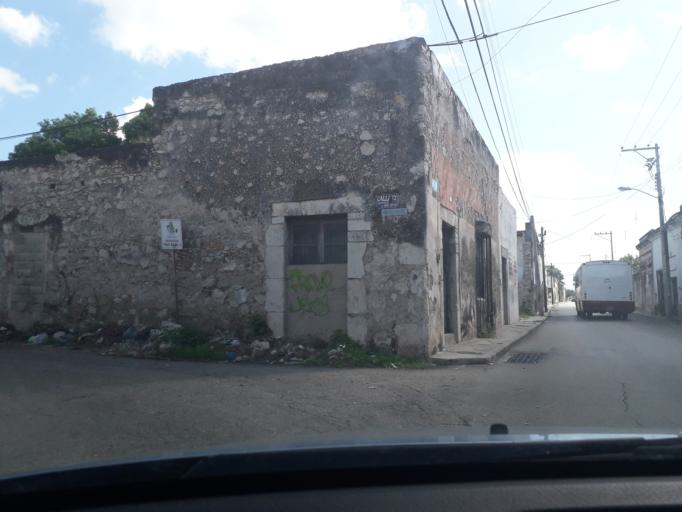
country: MX
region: Yucatan
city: Merida
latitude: 20.9589
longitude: -89.6233
